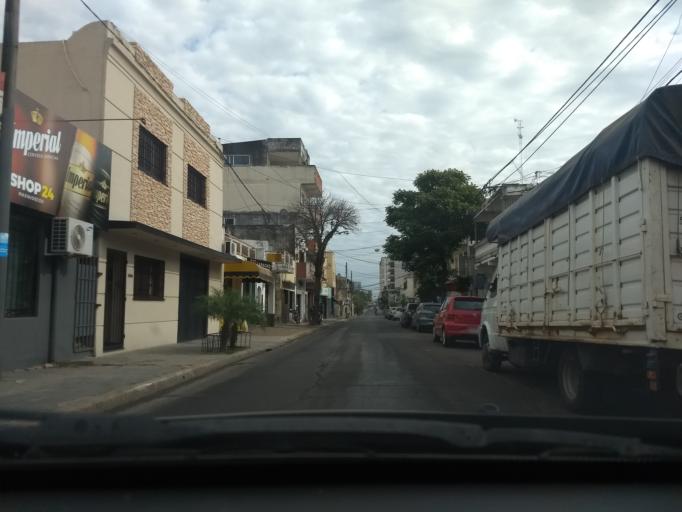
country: AR
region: Corrientes
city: Corrientes
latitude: -27.4686
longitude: -58.8254
